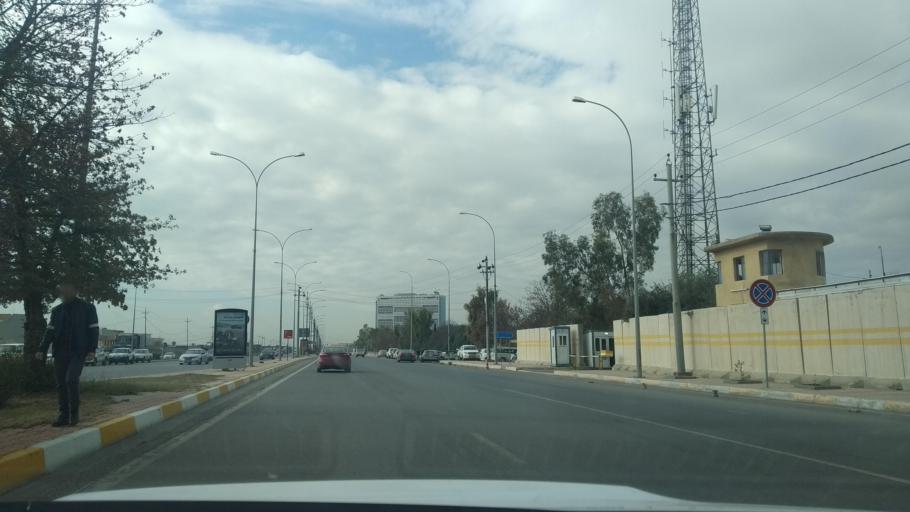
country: IQ
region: Arbil
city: Erbil
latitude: 36.1900
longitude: 43.9927
